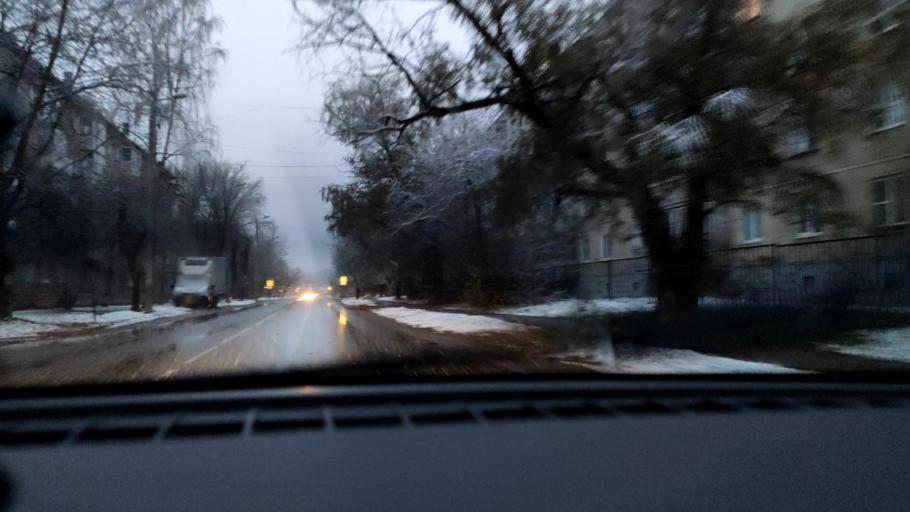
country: RU
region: Perm
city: Overyata
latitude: 58.0180
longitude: 55.9779
